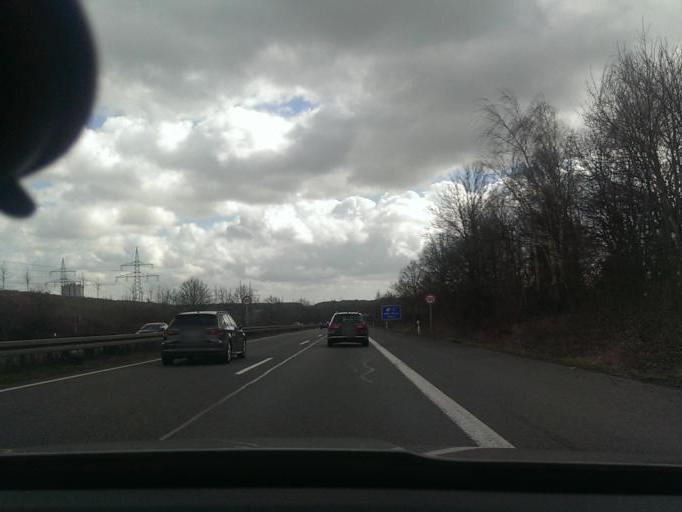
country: DE
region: Lower Saxony
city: Wolfsburg
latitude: 52.3986
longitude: 10.7348
